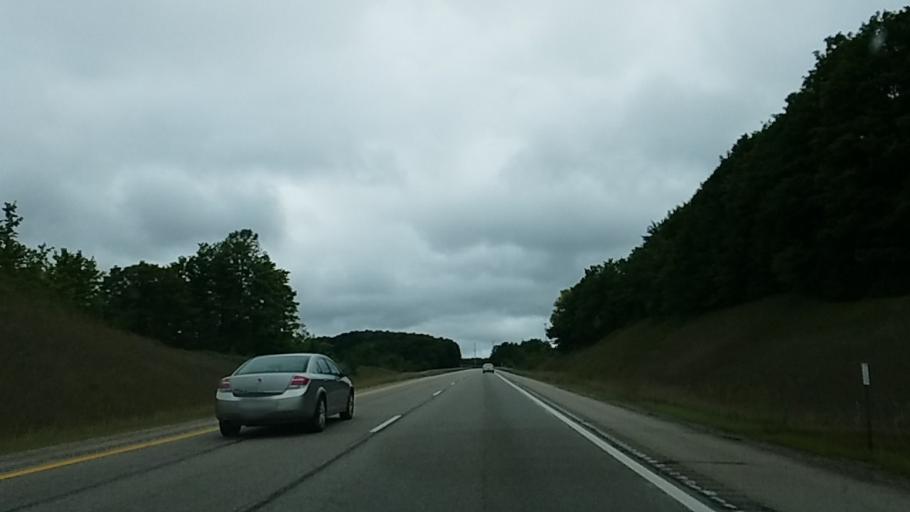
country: US
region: Michigan
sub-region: Otsego County
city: Gaylord
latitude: 45.1186
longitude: -84.6776
